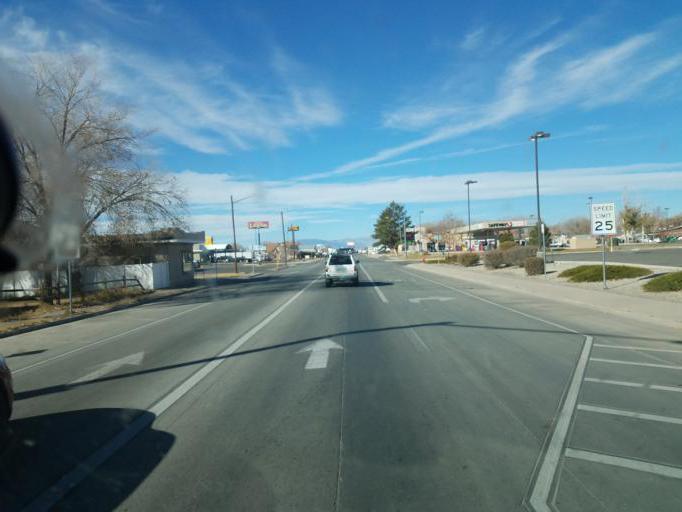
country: US
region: Colorado
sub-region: Alamosa County
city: Alamosa
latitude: 37.4682
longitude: -105.8743
